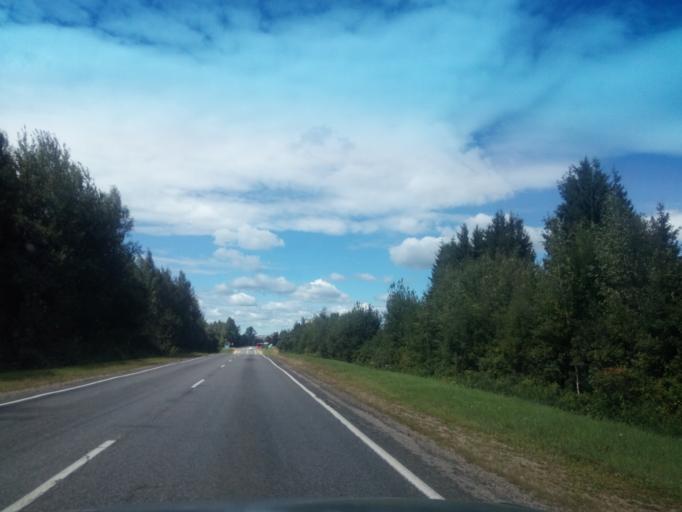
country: BY
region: Vitebsk
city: Polatsk
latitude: 55.5055
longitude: 28.7282
